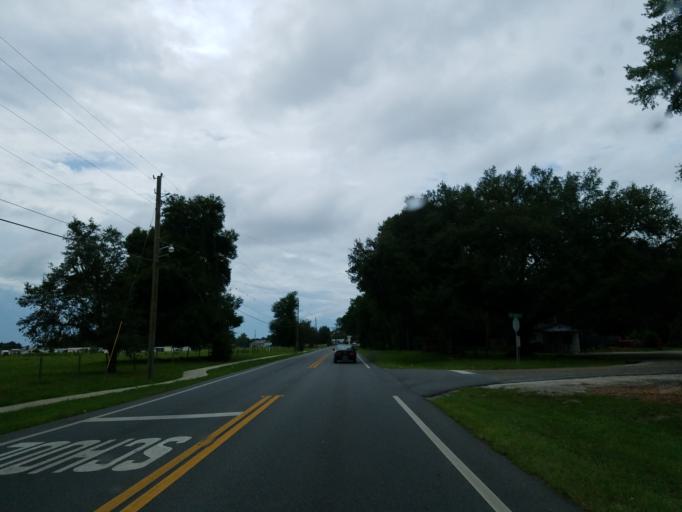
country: US
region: Florida
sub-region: Sumter County
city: Lake Panasoffkee
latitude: 28.7718
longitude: -82.1213
